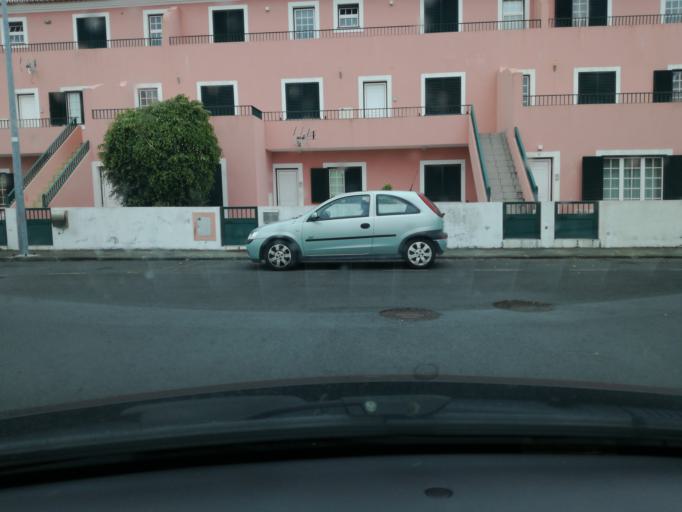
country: PT
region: Azores
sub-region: Angra do Heroismo
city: Angra do Heroismo
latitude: 38.6702
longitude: -27.2143
